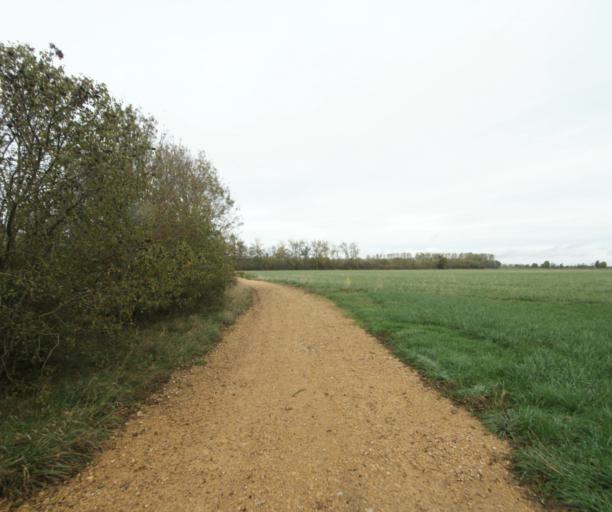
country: FR
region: Rhone-Alpes
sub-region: Departement de l'Ain
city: Pont-de-Vaux
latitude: 46.4568
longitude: 4.9030
